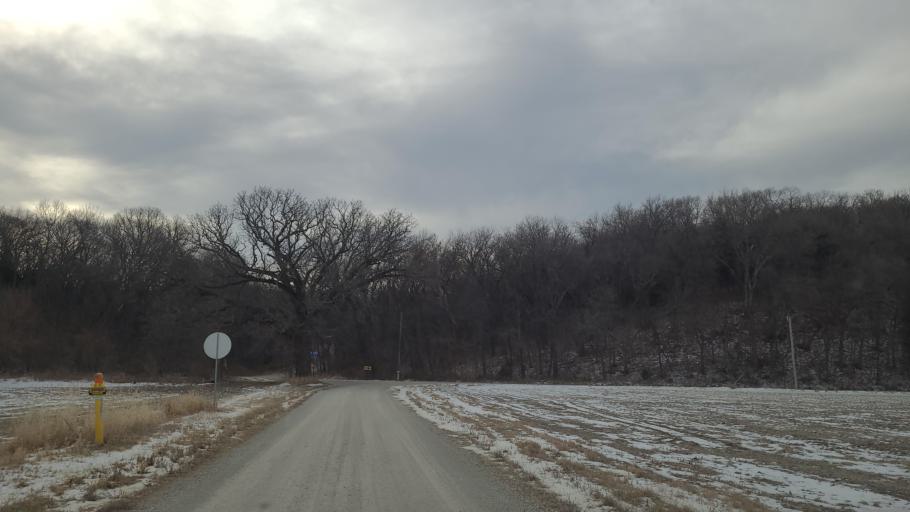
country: US
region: Kansas
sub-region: Jefferson County
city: Oskaloosa
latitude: 39.0589
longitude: -95.4612
